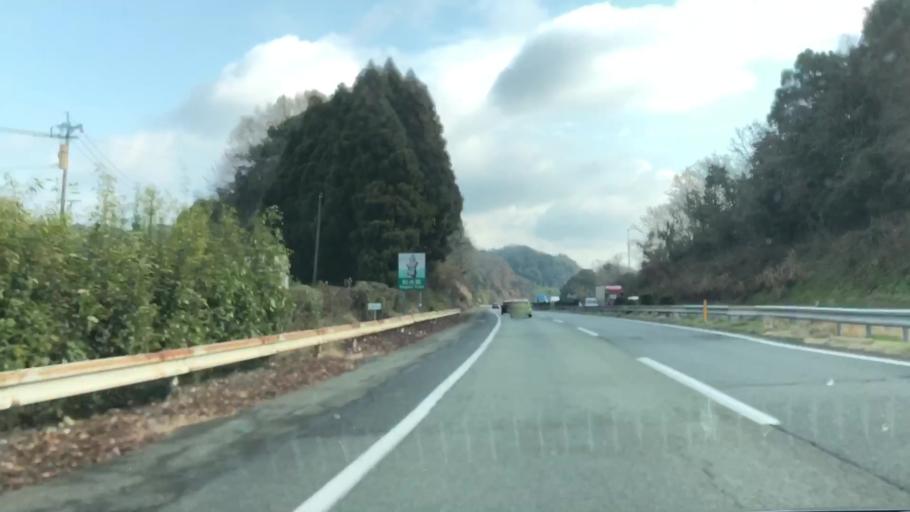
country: JP
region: Kumamoto
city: Tamana
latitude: 33.0026
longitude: 130.5860
